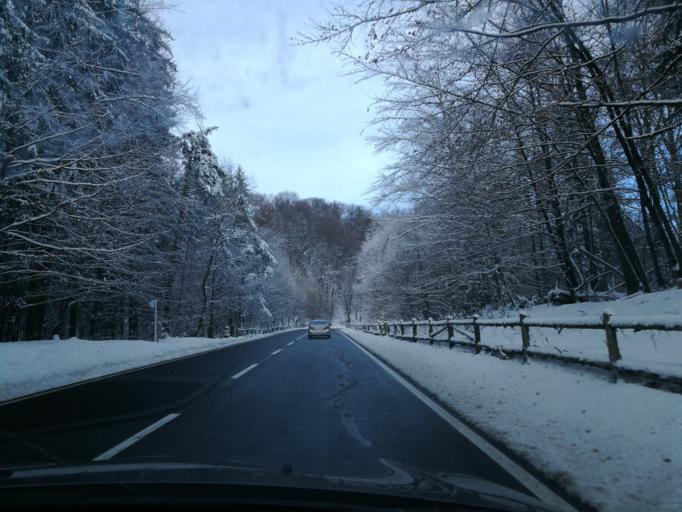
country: RO
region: Brasov
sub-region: Comuna Ghimbav
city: Ghimbav
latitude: 45.6189
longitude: 25.5437
